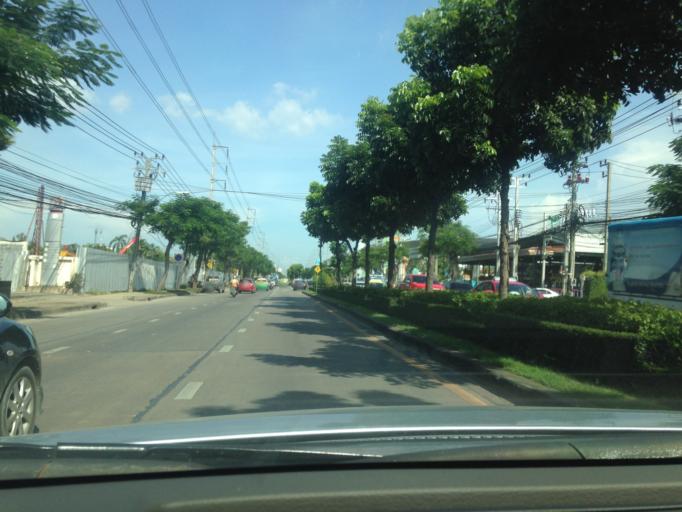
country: TH
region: Bangkok
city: Lat Krabang
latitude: 13.7222
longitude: 100.7260
